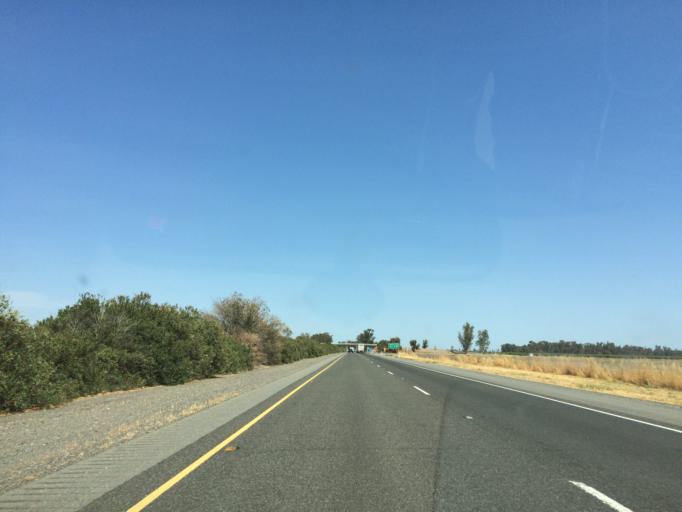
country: US
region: California
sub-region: Glenn County
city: Willows
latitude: 39.5770
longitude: -122.2111
